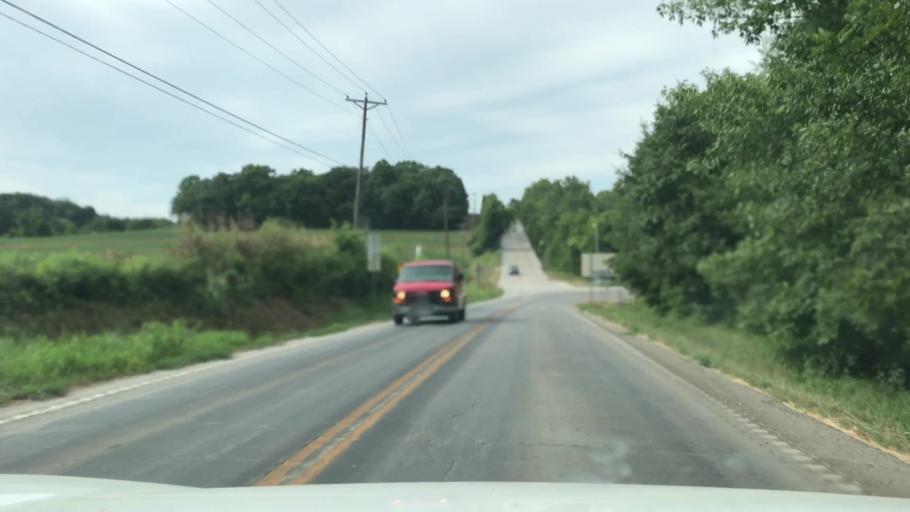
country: US
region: Missouri
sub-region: Saint Charles County
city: Weldon Spring
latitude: 38.6518
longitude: -90.7762
